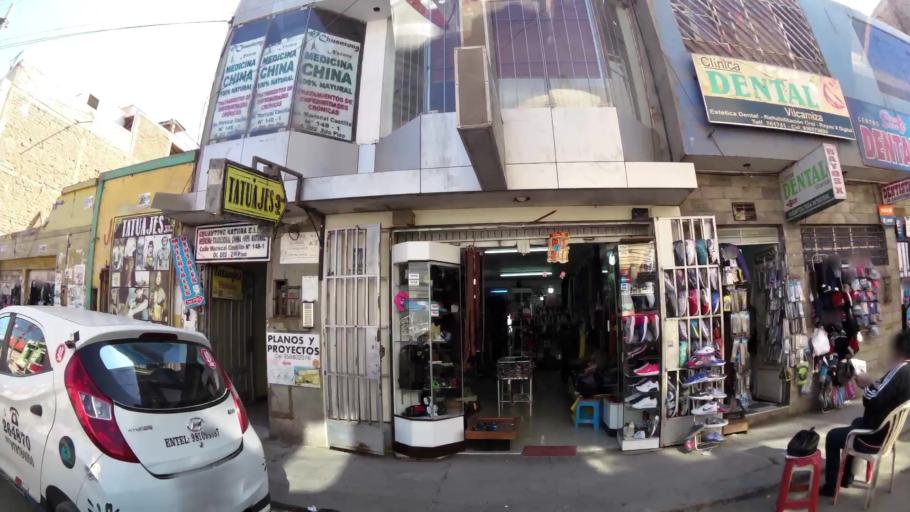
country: PE
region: Ica
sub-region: Provincia de Chincha
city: Chincha Alta
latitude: -13.4168
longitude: -76.1356
